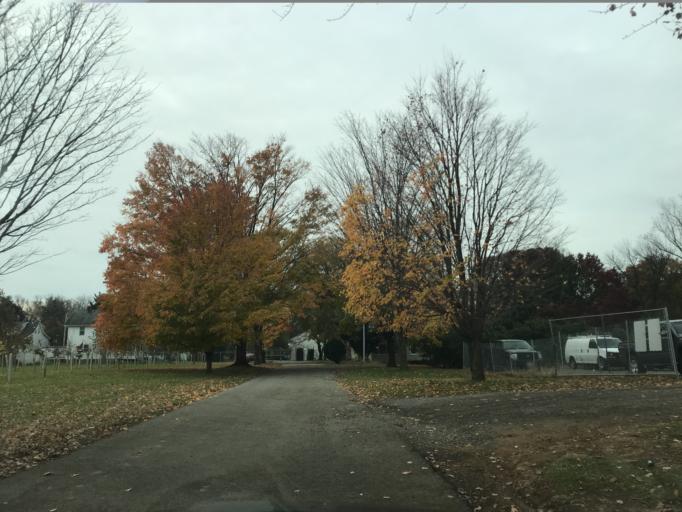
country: US
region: Maryland
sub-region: Baltimore County
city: Overlea
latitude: 39.3618
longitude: -76.5337
